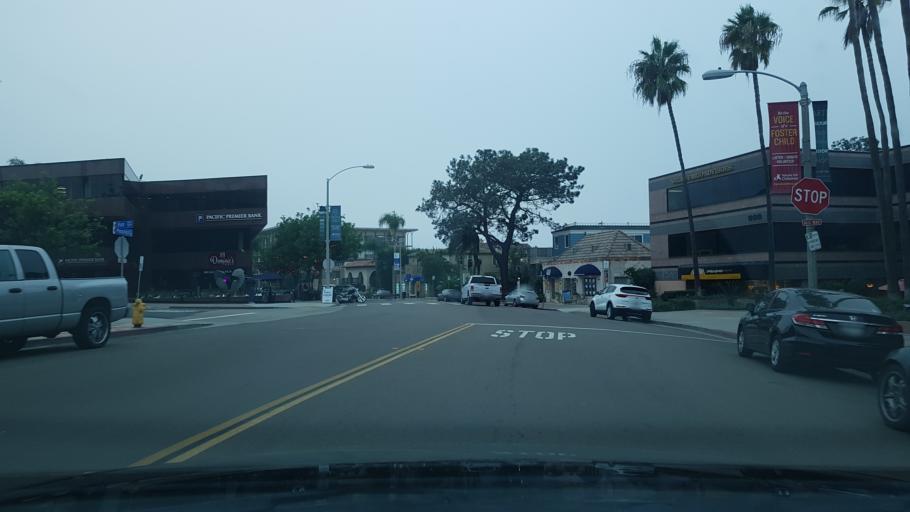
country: US
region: California
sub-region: San Diego County
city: La Jolla
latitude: 32.8465
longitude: -117.2754
